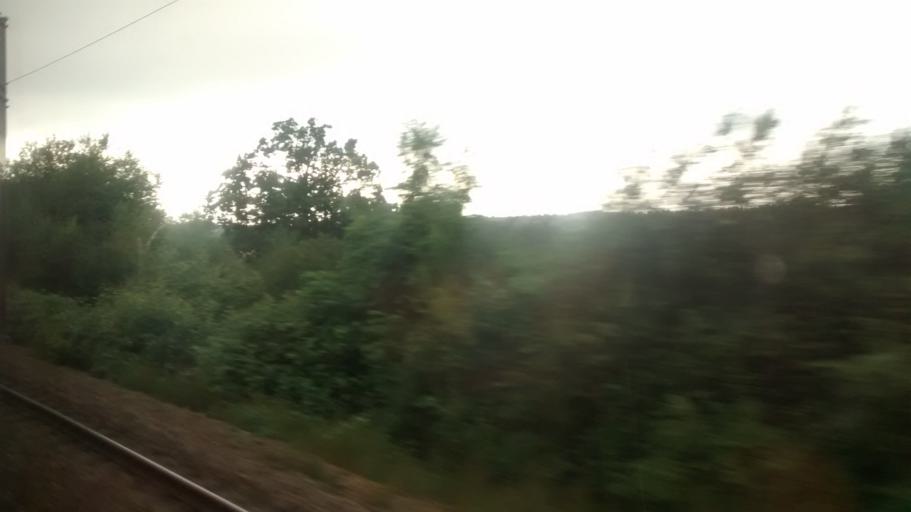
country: FR
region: Brittany
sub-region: Departement d'Ille-et-Vilaine
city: Vitre
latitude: 48.1242
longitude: -1.1814
